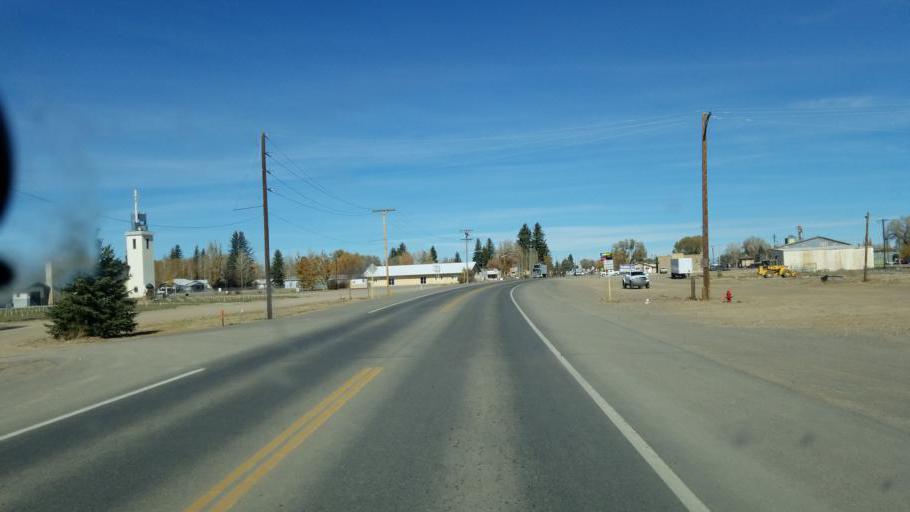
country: US
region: Colorado
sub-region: Conejos County
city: Conejos
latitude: 37.2706
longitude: -105.9628
